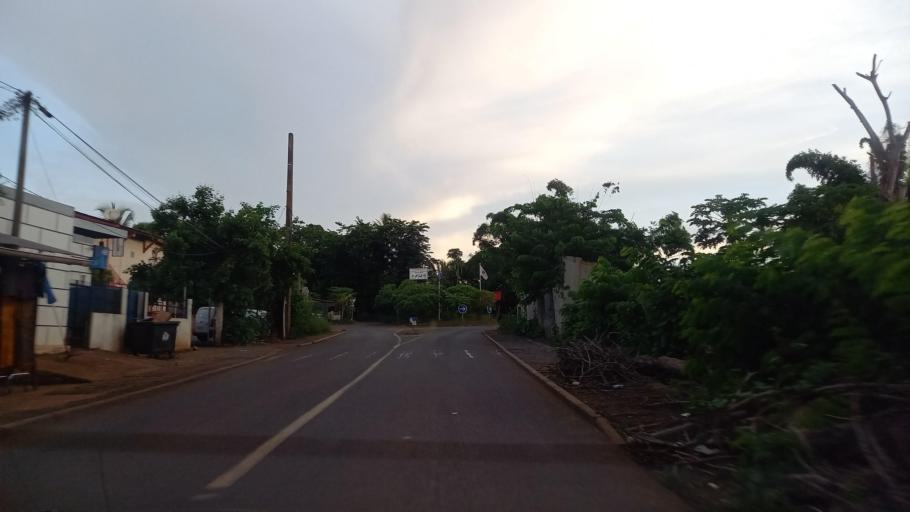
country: YT
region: Tsingoni
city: Tsingoni
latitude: -12.7897
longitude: 45.1123
